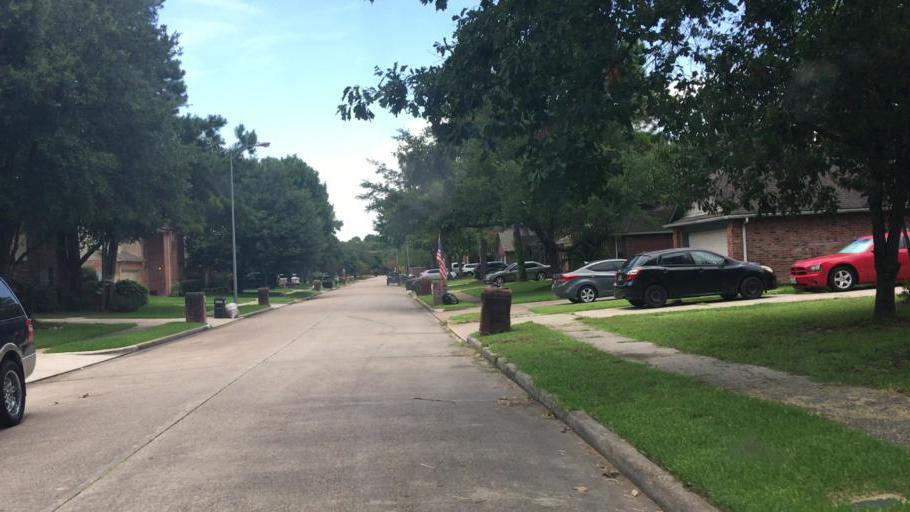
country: US
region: Texas
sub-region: Harris County
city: Atascocita
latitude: 29.9932
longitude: -95.1730
